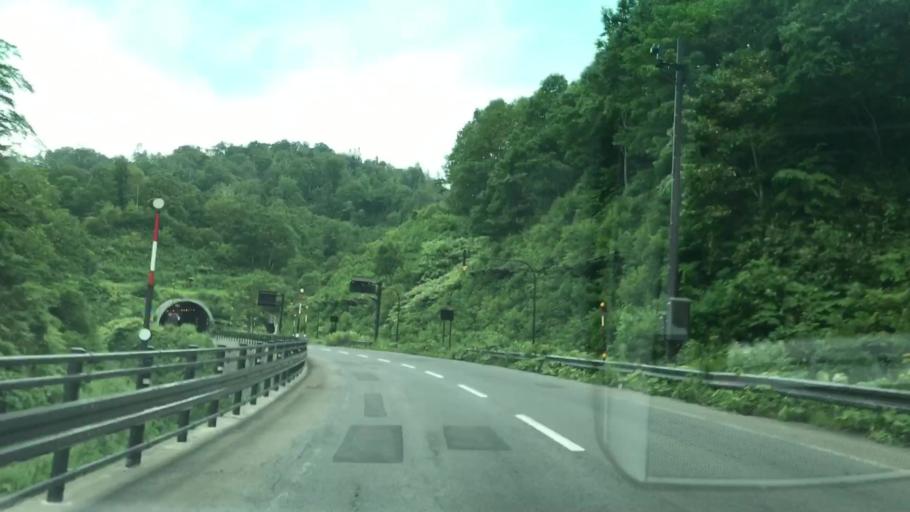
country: JP
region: Hokkaido
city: Yoichi
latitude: 42.9824
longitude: 140.8719
